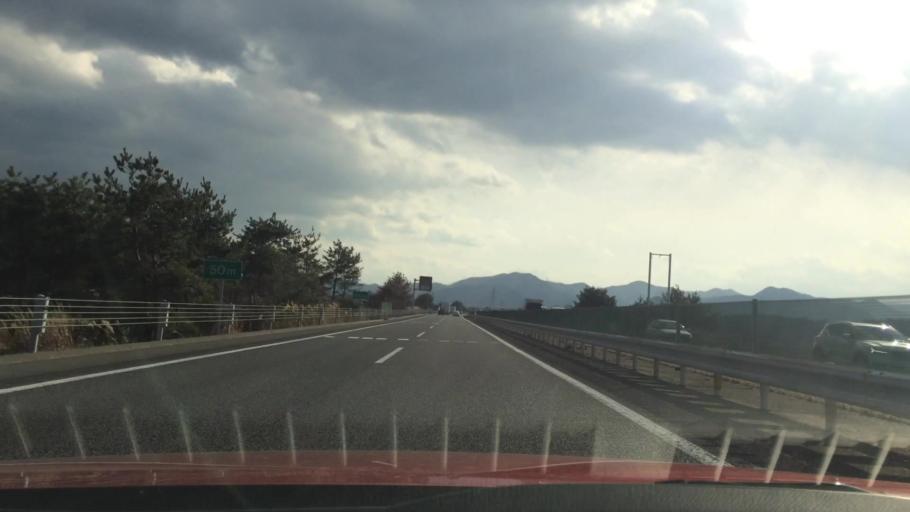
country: JP
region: Nagano
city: Shiojiri
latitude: 36.1547
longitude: 137.9681
